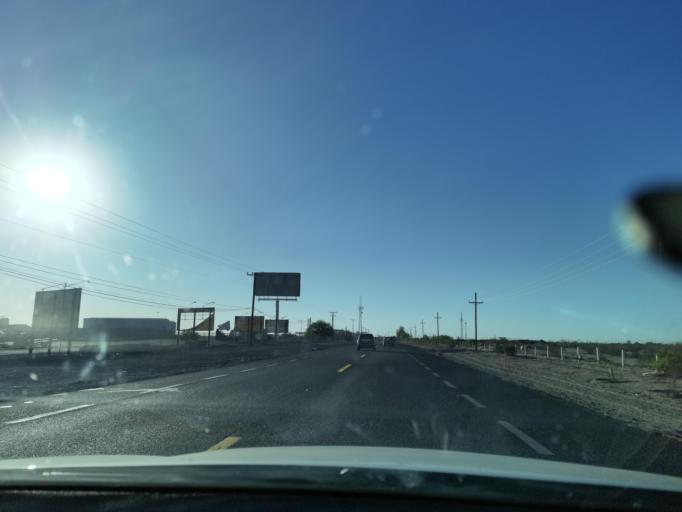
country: MX
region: Baja California
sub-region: Mexicali
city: Islas Agrarias Grupo A
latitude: 32.6312
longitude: -115.2619
